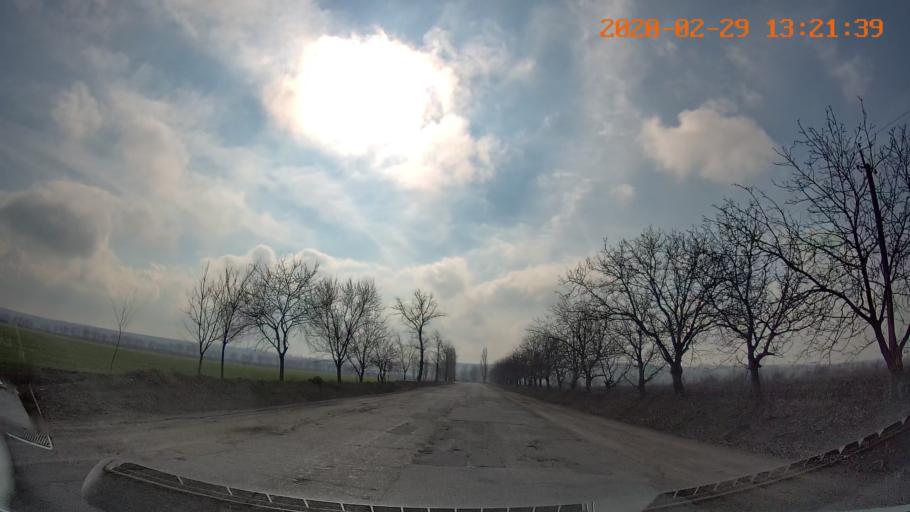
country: MD
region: Telenesti
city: Camenca
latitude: 47.9683
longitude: 28.6310
